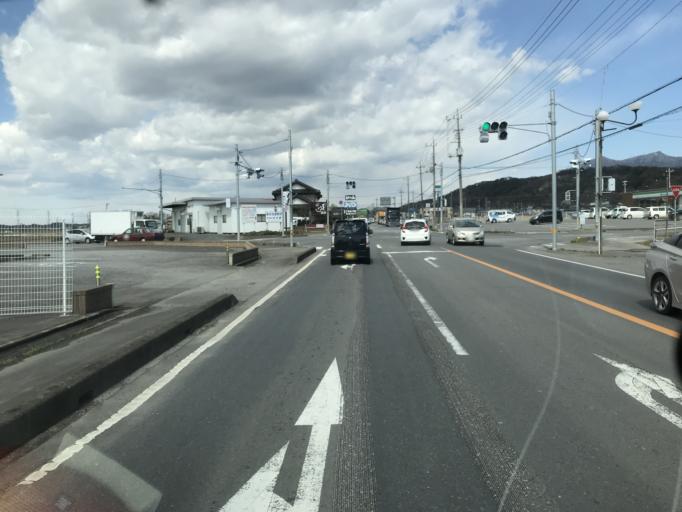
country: JP
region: Ibaraki
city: Tsukuba
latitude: 36.1449
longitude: 140.1195
